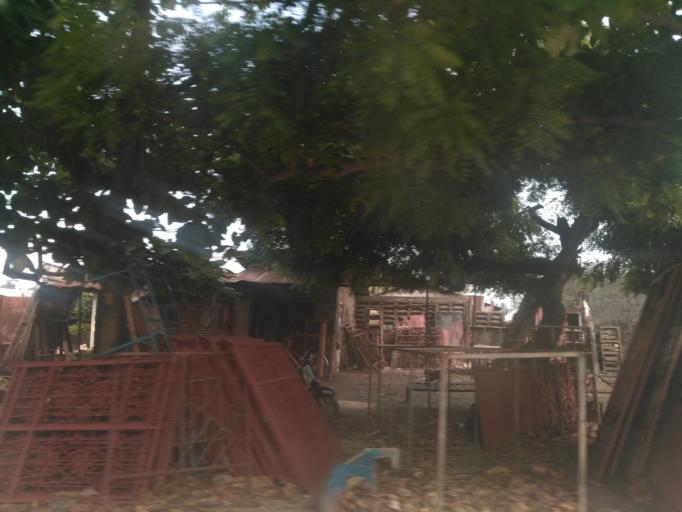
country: TZ
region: Zanzibar Urban/West
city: Zanzibar
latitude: -6.1694
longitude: 39.2085
